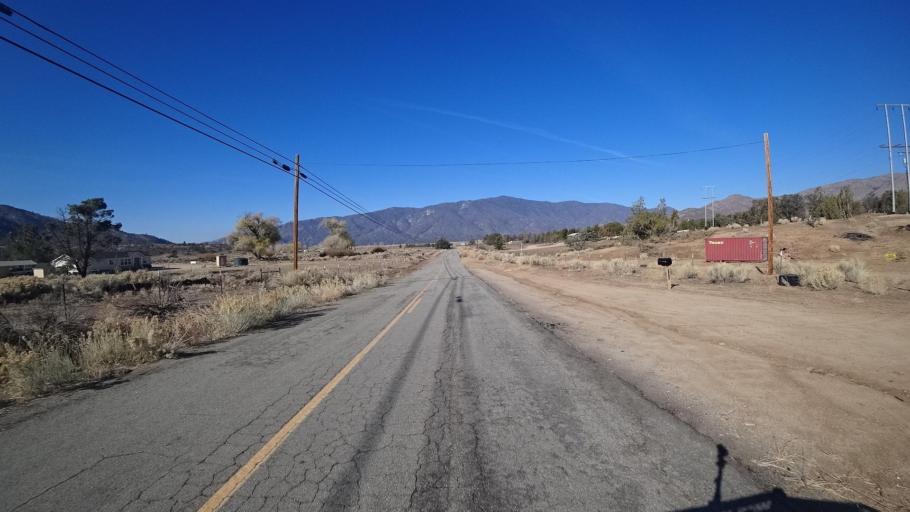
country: US
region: California
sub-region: Kern County
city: Bodfish
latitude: 35.4039
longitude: -118.4847
